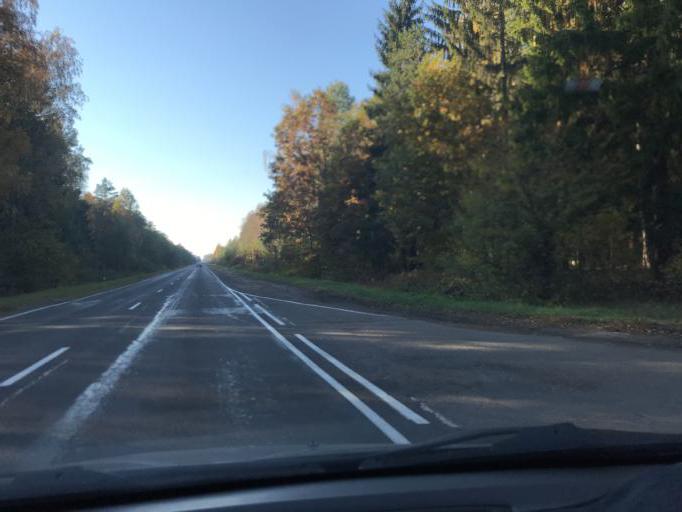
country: BY
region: Minsk
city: Staryya Darohi
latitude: 53.0409
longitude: 28.1683
